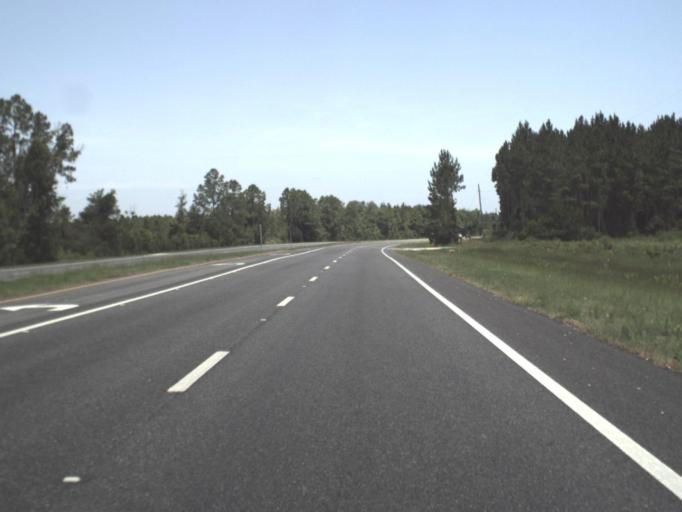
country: US
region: Florida
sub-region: Taylor County
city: Steinhatchee
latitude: 29.7181
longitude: -83.3046
